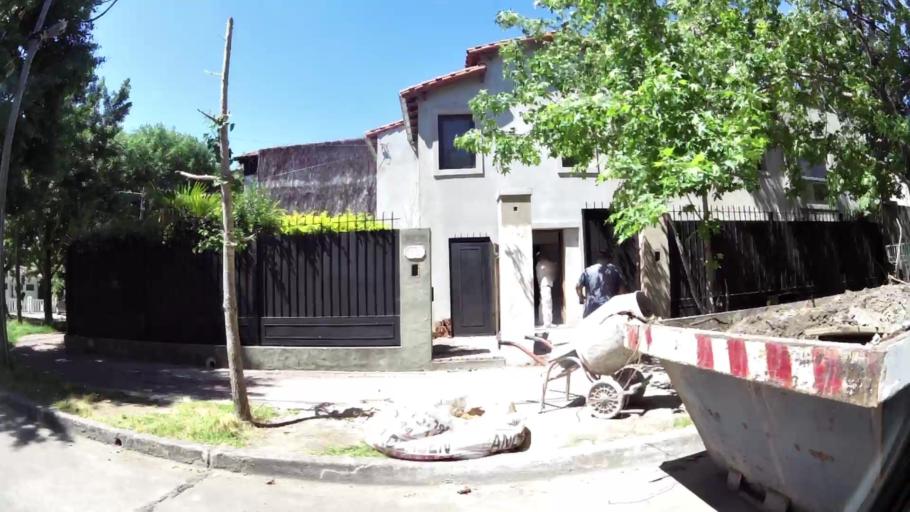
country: AR
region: Buenos Aires
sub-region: Partido de San Isidro
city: San Isidro
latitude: -34.4763
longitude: -58.4952
